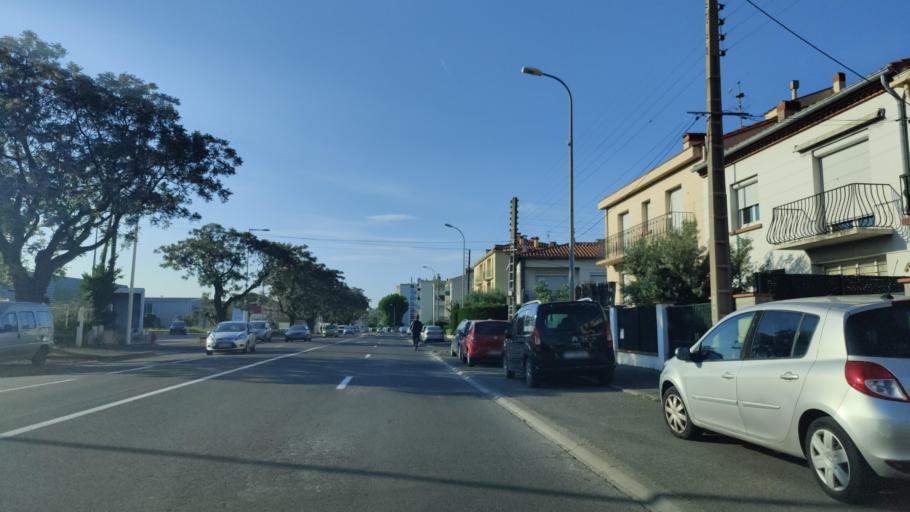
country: FR
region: Languedoc-Roussillon
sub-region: Departement des Pyrenees-Orientales
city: Perpignan
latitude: 42.7079
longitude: 2.8864
